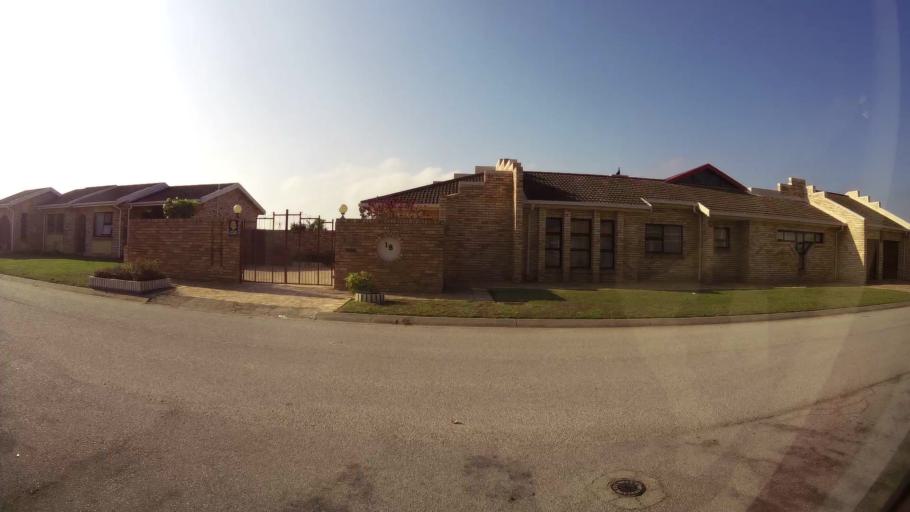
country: ZA
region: Eastern Cape
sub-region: Nelson Mandela Bay Metropolitan Municipality
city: Port Elizabeth
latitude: -33.9207
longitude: 25.5260
